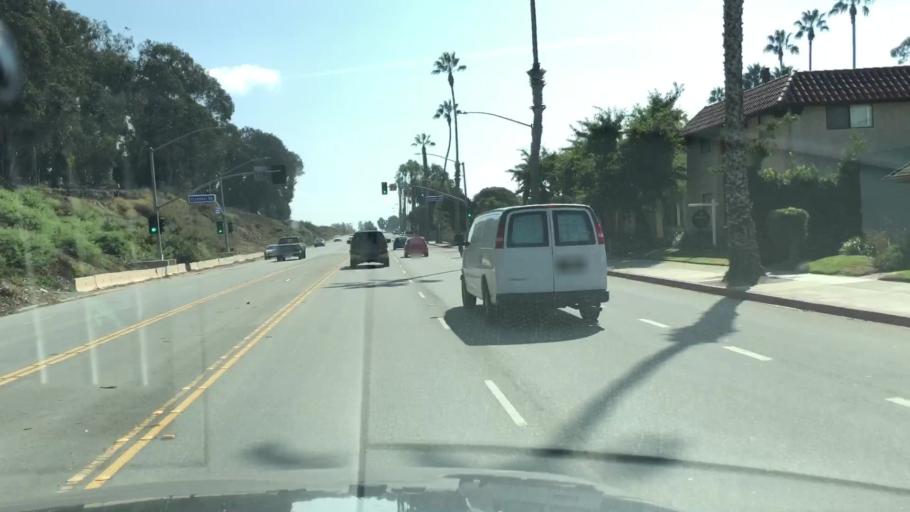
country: US
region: California
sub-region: Ventura County
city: Ventura
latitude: 34.2591
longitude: -119.2622
